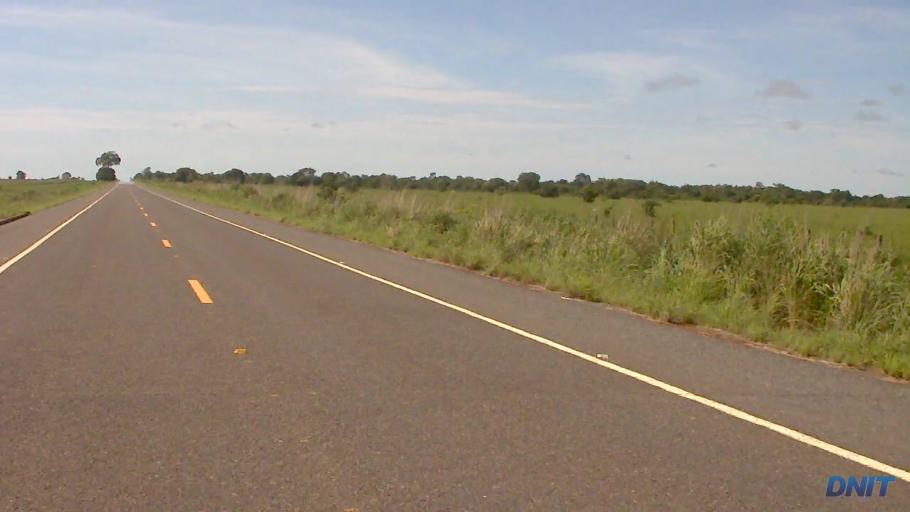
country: BR
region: Goias
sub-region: Sao Miguel Do Araguaia
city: Sao Miguel do Araguaia
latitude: -13.4200
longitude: -50.1295
